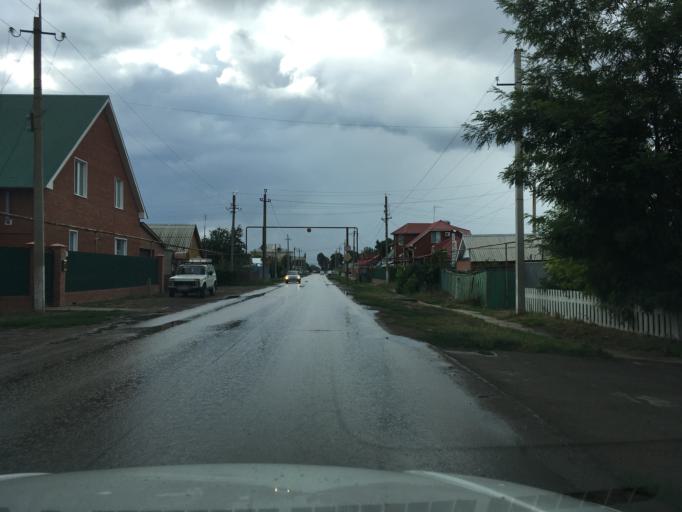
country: RU
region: Samara
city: Bezenchuk
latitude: 52.9801
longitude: 49.4363
